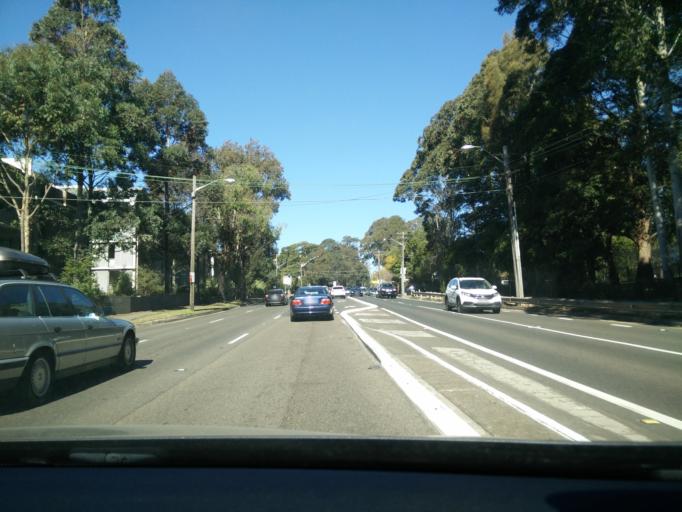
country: AU
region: New South Wales
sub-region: Ku-ring-gai
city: South Turramurra
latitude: -33.7297
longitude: 151.1230
